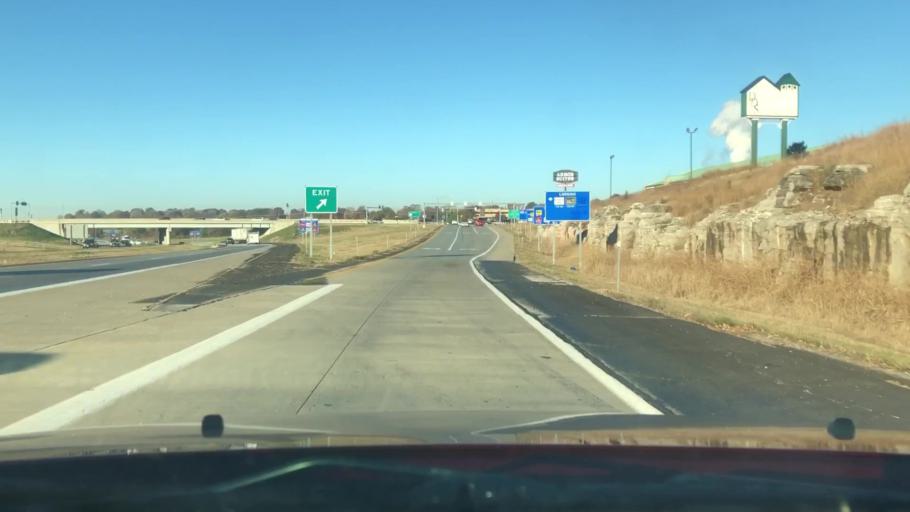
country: US
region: Missouri
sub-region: Greene County
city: Springfield
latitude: 37.1425
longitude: -93.2747
